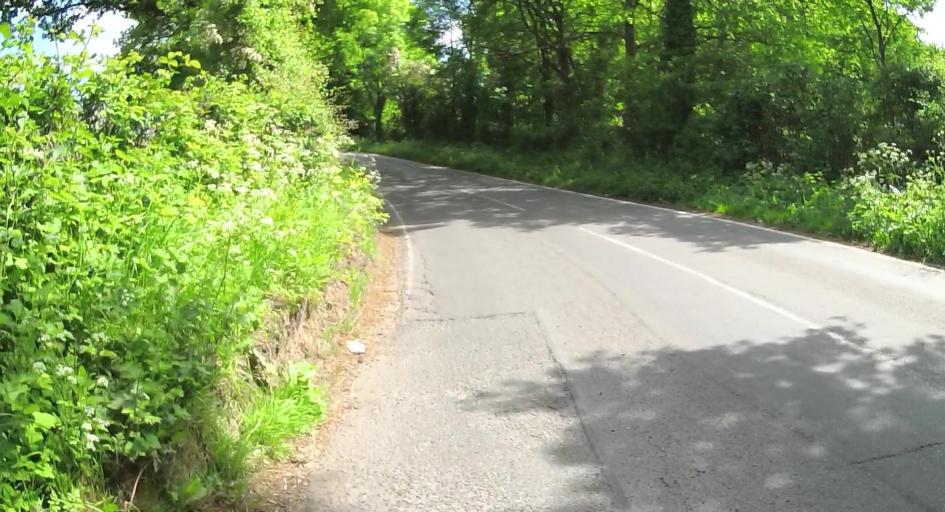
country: GB
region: England
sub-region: Surrey
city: Farnham
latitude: 51.2206
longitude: -0.8384
